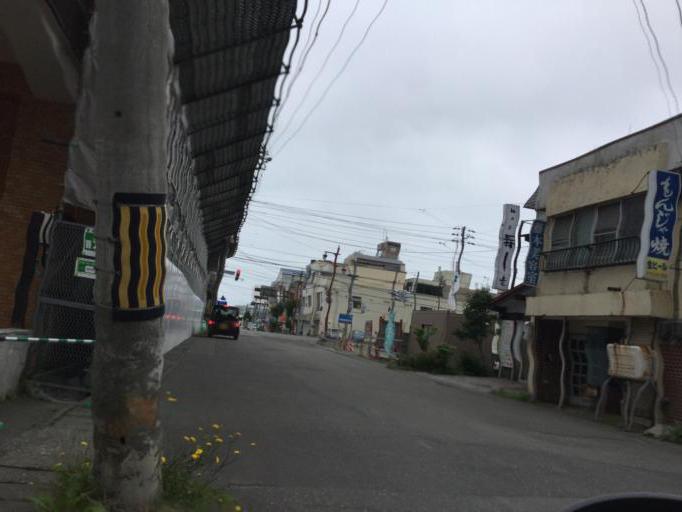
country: JP
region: Hokkaido
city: Wakkanai
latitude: 45.4173
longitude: 141.6731
